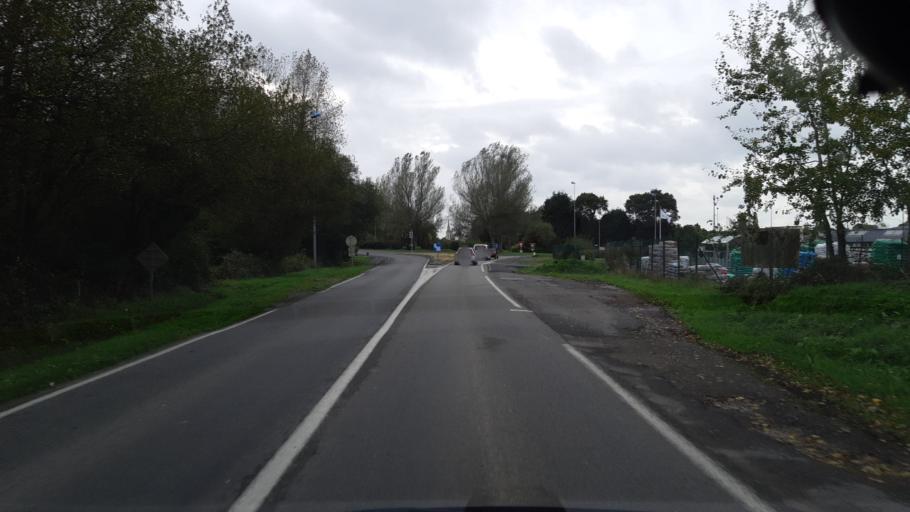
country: FR
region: Lower Normandy
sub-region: Departement de la Manche
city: Brehal
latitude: 48.9021
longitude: -1.4986
